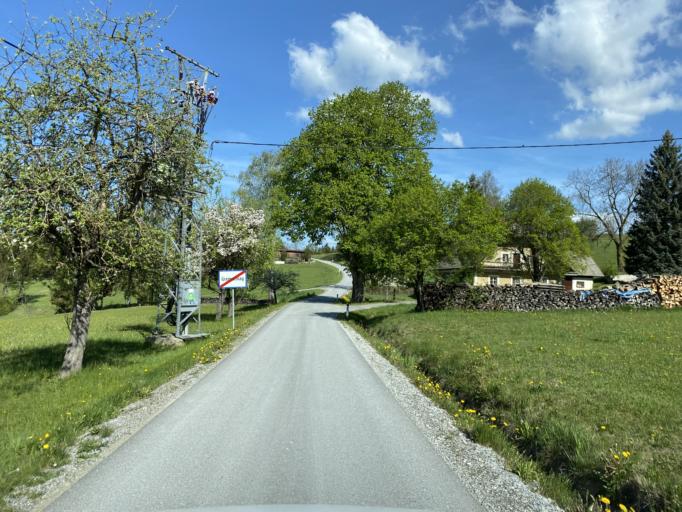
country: AT
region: Styria
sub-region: Politischer Bezirk Weiz
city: Strallegg
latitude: 47.3695
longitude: 15.7127
